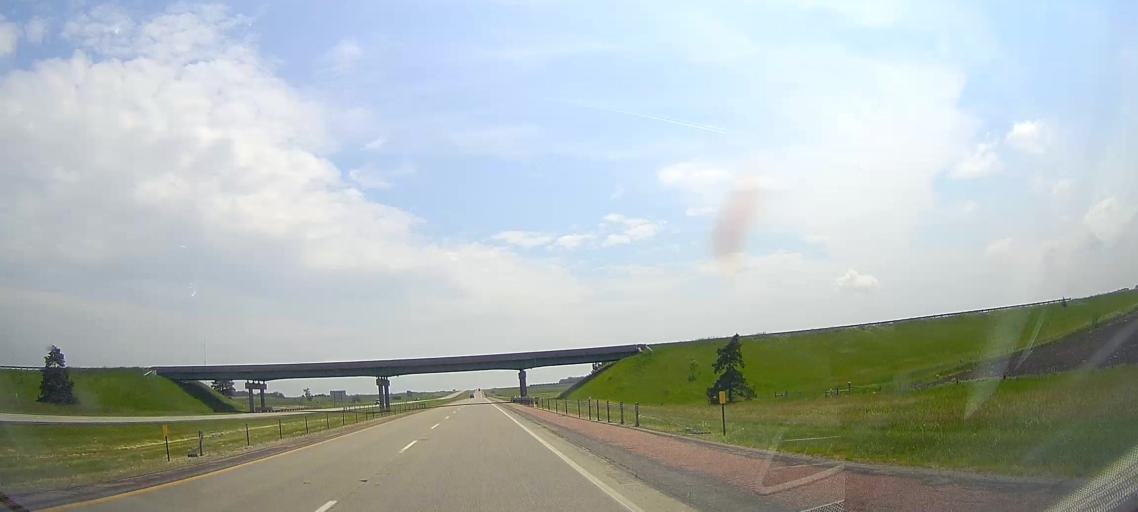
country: US
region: South Dakota
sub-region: Union County
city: Beresford
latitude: 43.0700
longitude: -96.7963
